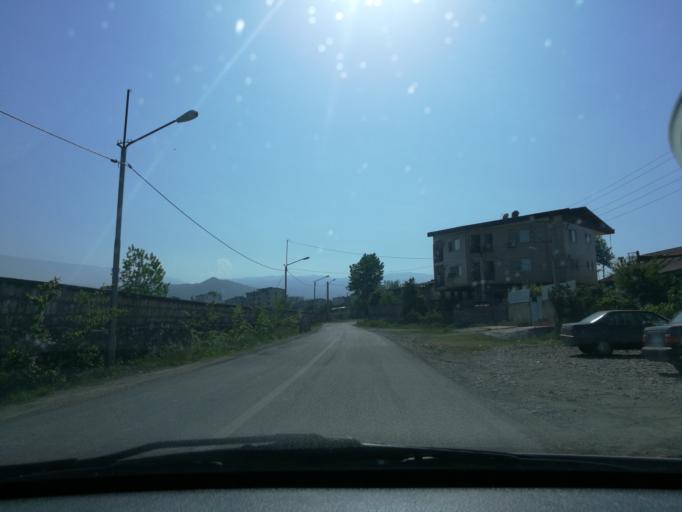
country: IR
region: Mazandaran
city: Chalus
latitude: 36.6564
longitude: 51.4277
